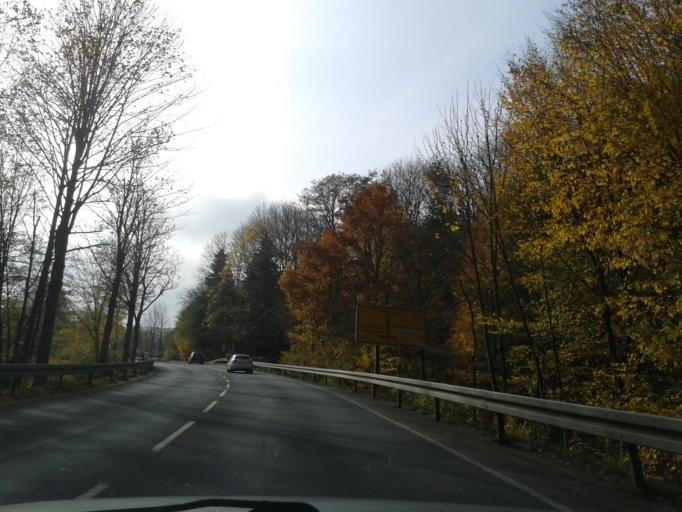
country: DE
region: North Rhine-Westphalia
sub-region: Regierungsbezirk Arnsberg
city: Olsberg
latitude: 51.3087
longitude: 8.5033
